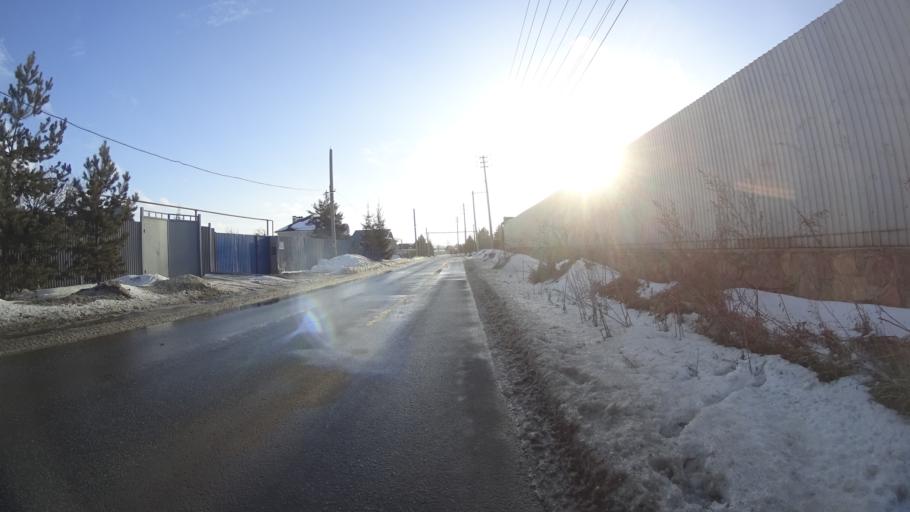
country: RU
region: Chelyabinsk
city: Sargazy
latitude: 55.1124
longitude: 61.2806
